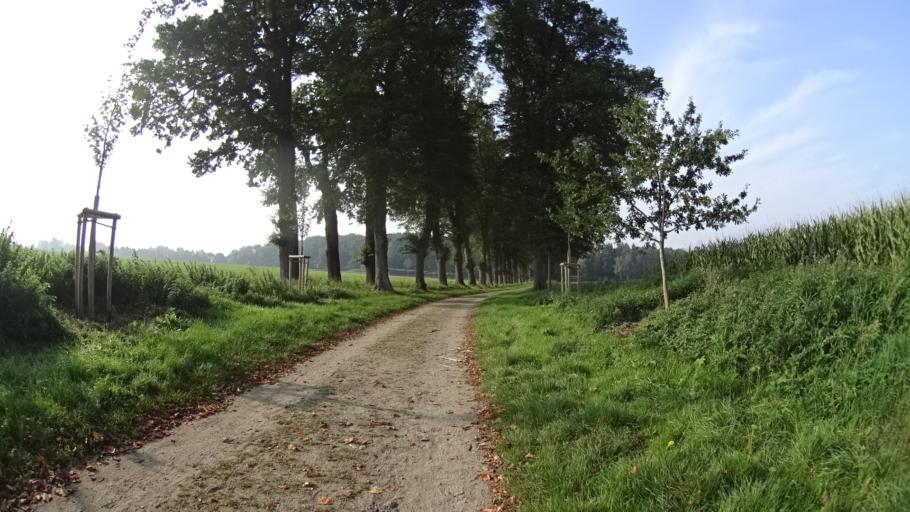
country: DE
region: Lower Saxony
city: Reppenstedt
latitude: 53.2392
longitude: 10.3788
